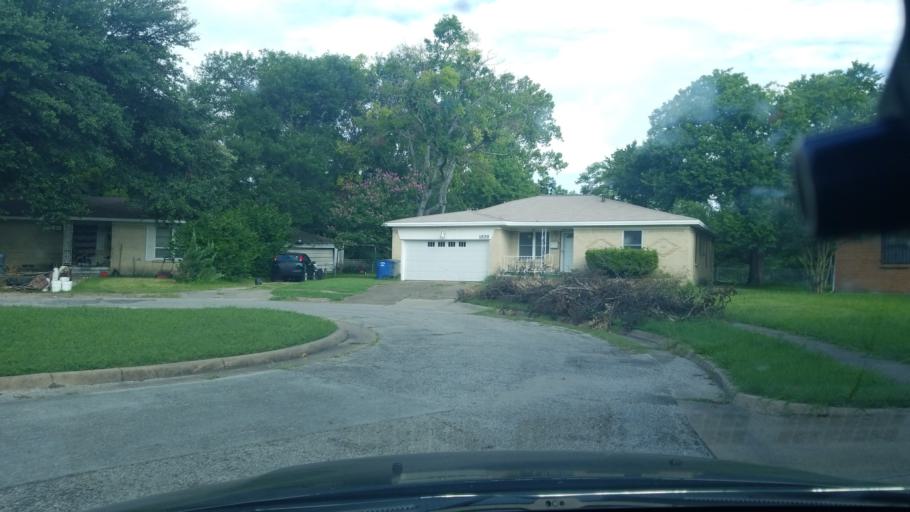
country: US
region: Texas
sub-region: Dallas County
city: Balch Springs
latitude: 32.7428
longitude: -96.6642
